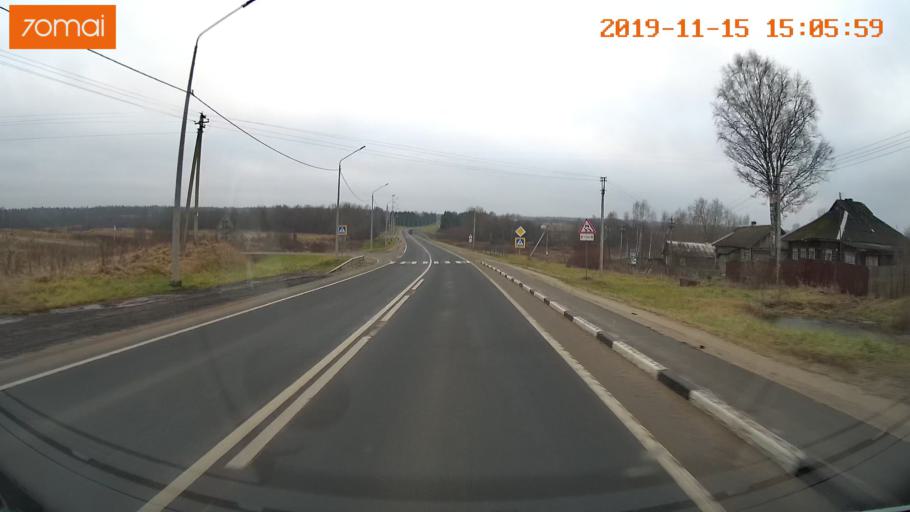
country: RU
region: Jaroslavl
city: Prechistoye
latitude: 58.3977
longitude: 40.3166
